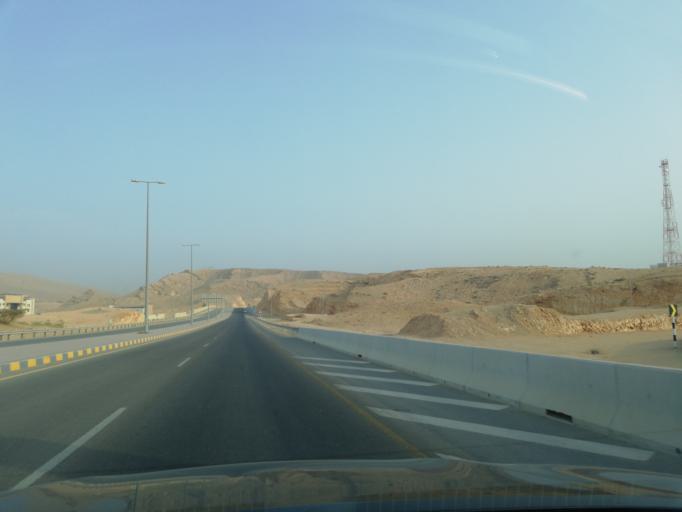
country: OM
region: Muhafazat Masqat
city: Bawshar
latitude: 23.5508
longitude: 58.2926
